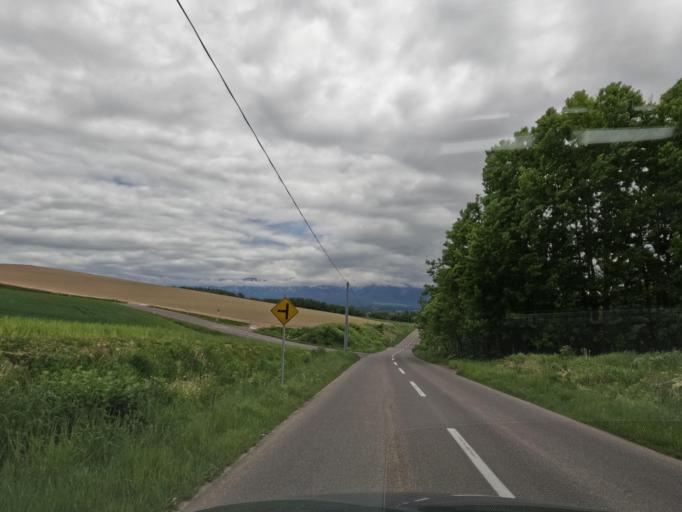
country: JP
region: Hokkaido
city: Shimo-furano
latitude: 43.4883
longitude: 142.4209
